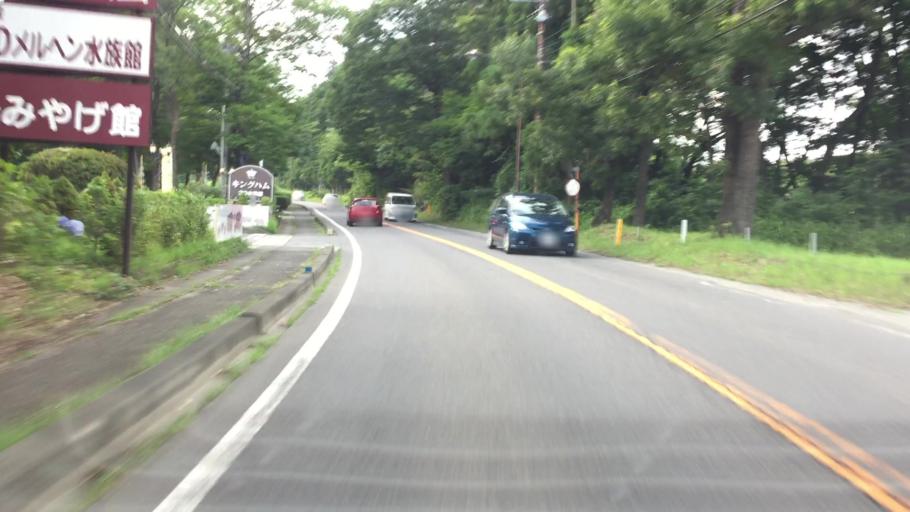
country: JP
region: Tochigi
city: Kuroiso
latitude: 37.0143
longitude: 140.0310
